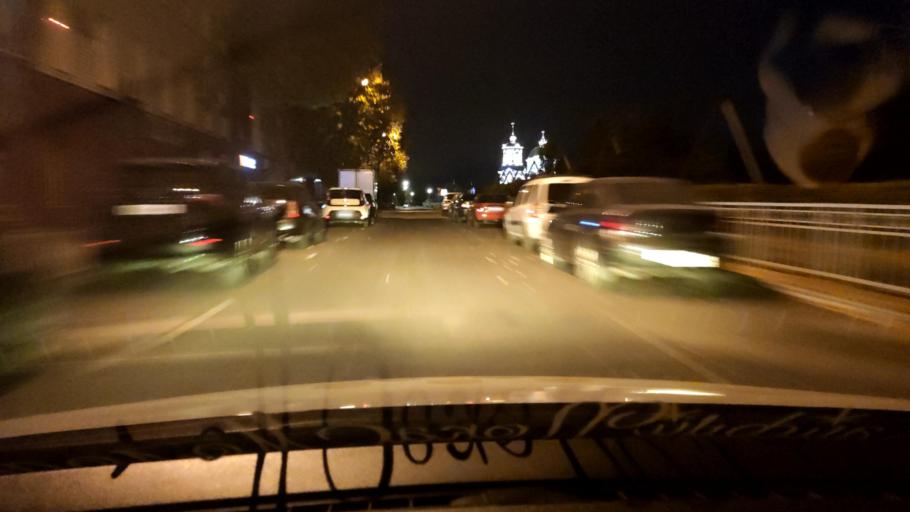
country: RU
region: Voronezj
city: Voronezh
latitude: 51.6634
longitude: 39.2103
